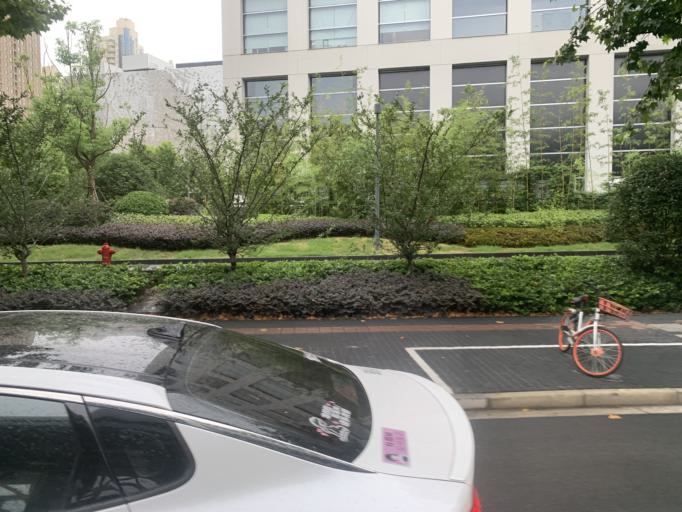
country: CN
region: Shanghai Shi
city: Luwan
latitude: 31.2129
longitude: 121.4736
